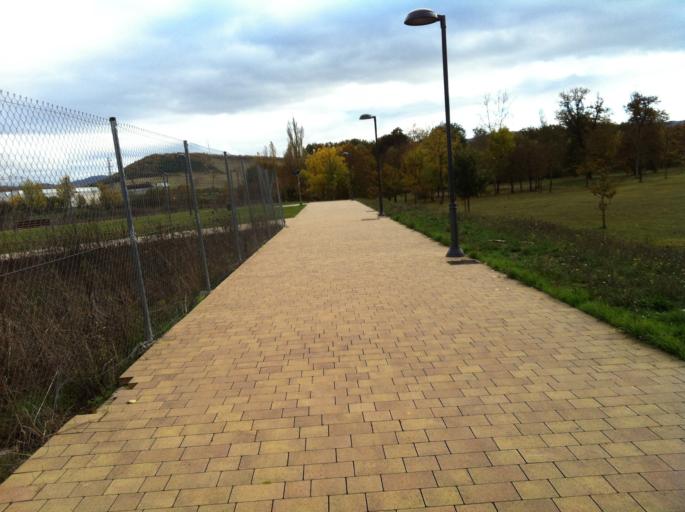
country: ES
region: Basque Country
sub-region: Provincia de Alava
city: Gasteiz / Vitoria
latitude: 42.8301
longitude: -2.6593
